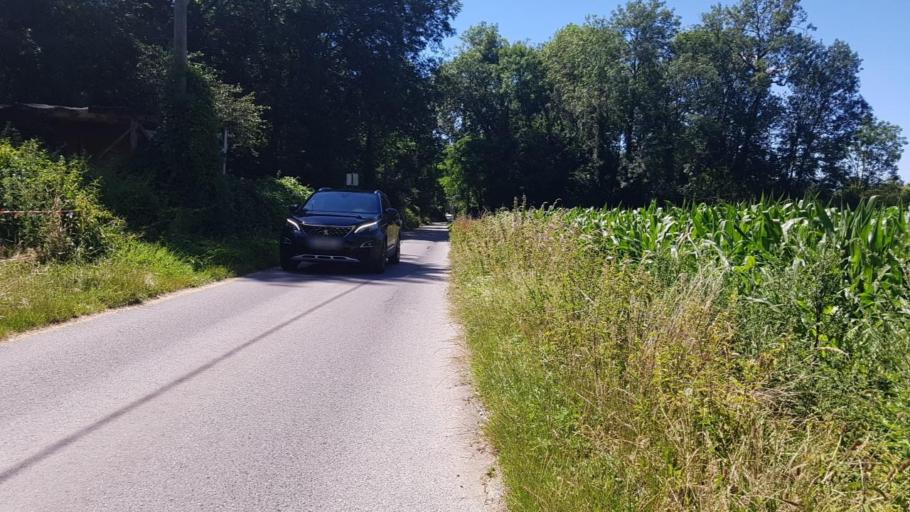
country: FR
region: Ile-de-France
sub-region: Departement de Seine-et-Marne
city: Nanteuil-les-Meaux
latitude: 48.9343
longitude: 2.9024
